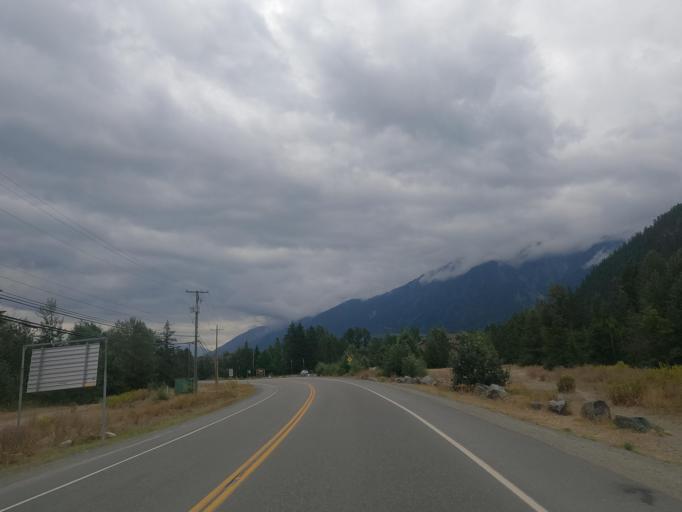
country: CA
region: British Columbia
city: Pemberton
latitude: 50.3163
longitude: -122.7955
